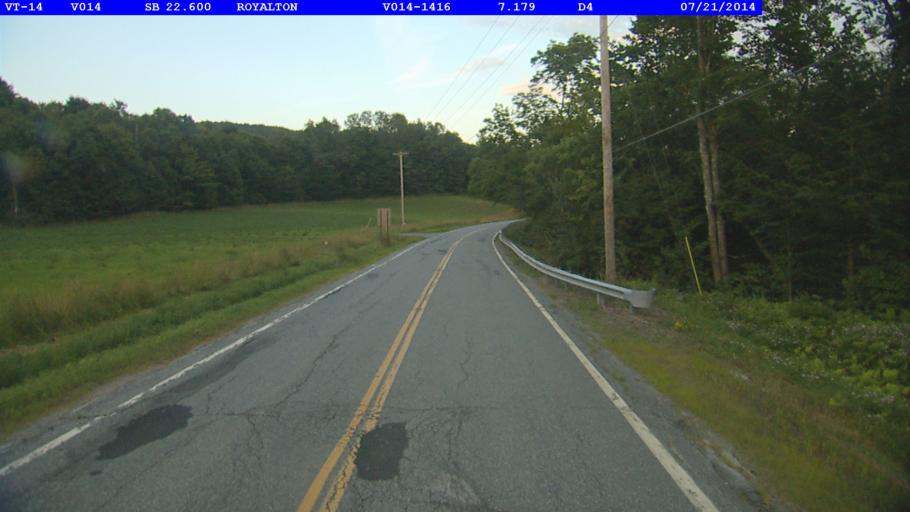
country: US
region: Vermont
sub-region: Orange County
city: Randolph
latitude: 43.8403
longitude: -72.5821
